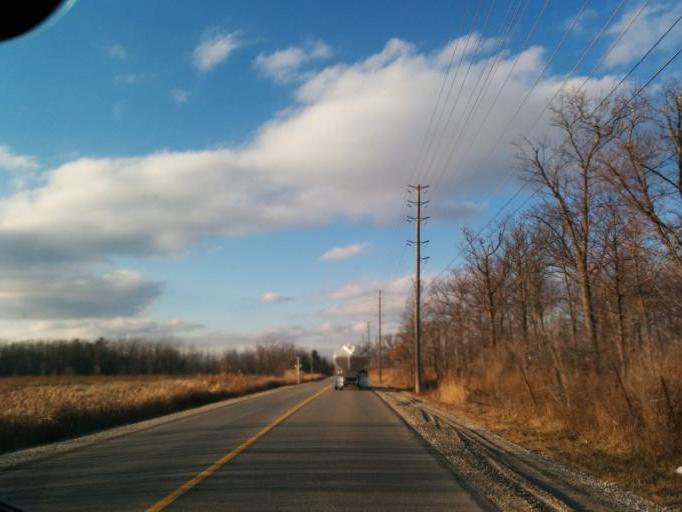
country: CA
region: Ontario
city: Oakville
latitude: 43.5163
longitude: -79.7081
